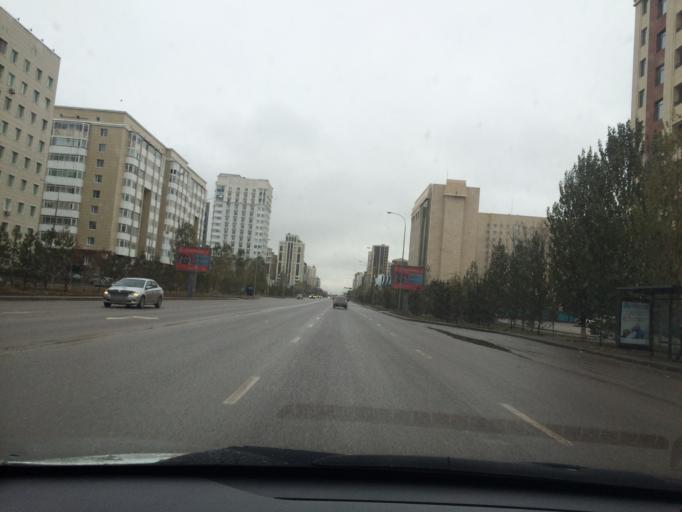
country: KZ
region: Astana Qalasy
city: Astana
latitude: 51.1151
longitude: 71.4184
